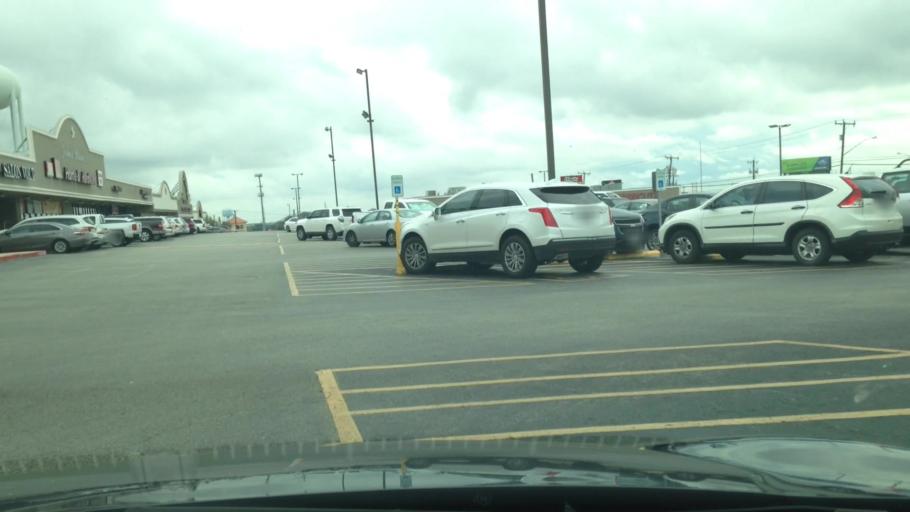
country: US
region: Texas
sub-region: Bexar County
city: Castle Hills
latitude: 29.5446
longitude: -98.5284
